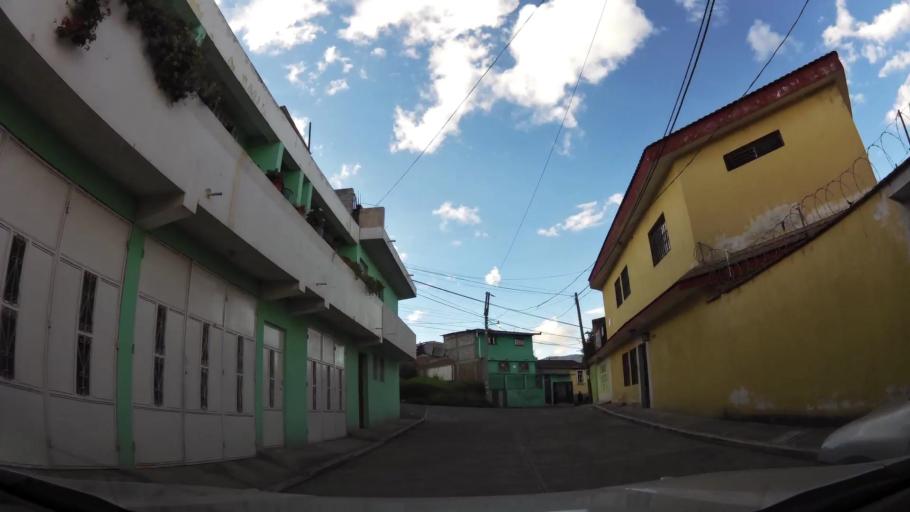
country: GT
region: Quetzaltenango
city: Quetzaltenango
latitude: 14.8522
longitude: -91.5261
